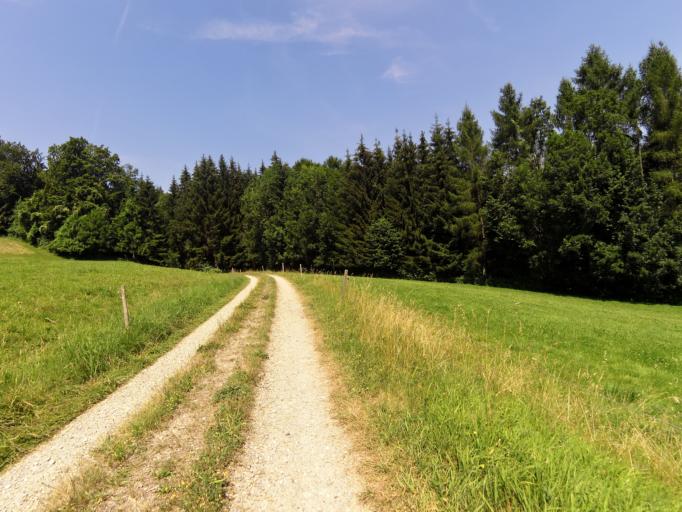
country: CH
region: Thurgau
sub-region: Frauenfeld District
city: Thundorf
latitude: 47.5644
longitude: 8.9943
